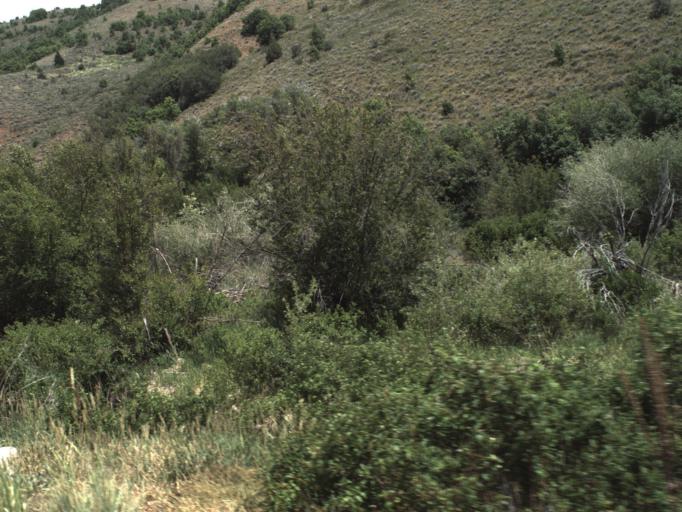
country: US
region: Utah
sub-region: Weber County
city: Wolf Creek
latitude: 41.3322
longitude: -111.6096
